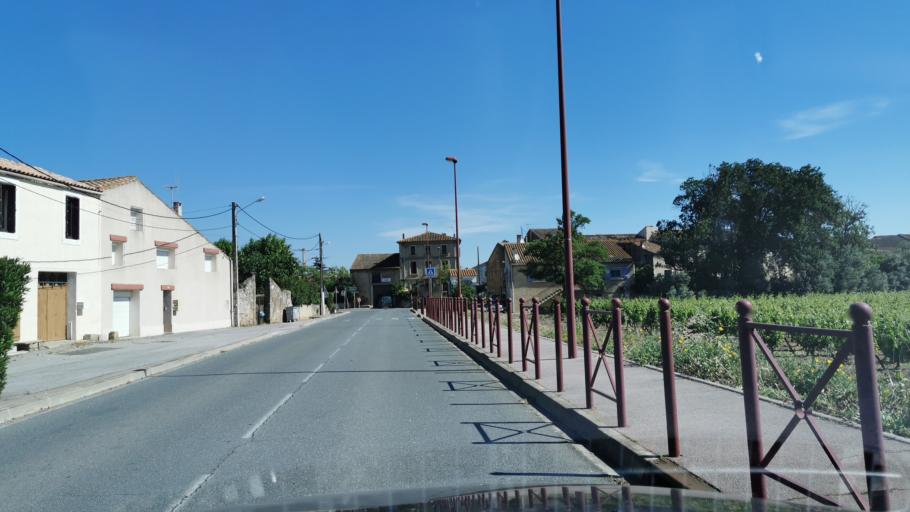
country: FR
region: Languedoc-Roussillon
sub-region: Departement de l'Aude
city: Canet
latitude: 43.2146
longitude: 2.8629
